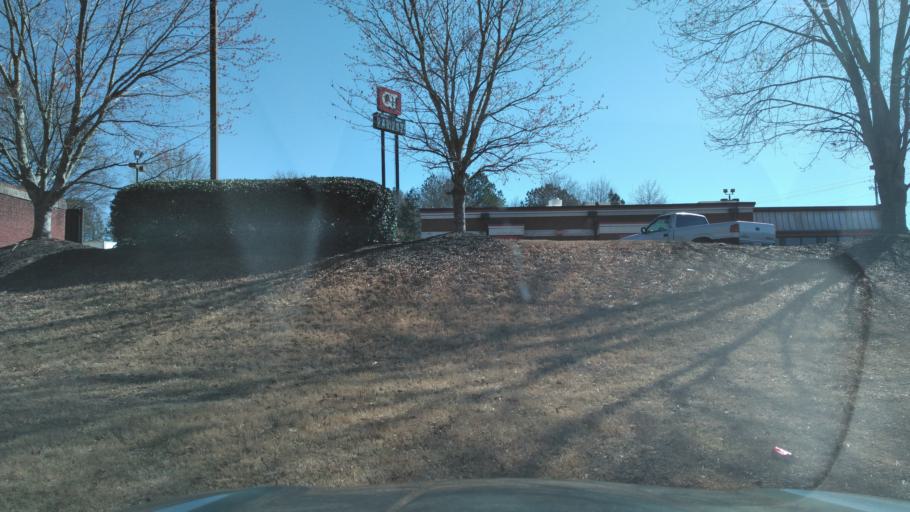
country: US
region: Georgia
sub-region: Jackson County
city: Jefferson
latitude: 34.1532
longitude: -83.6501
